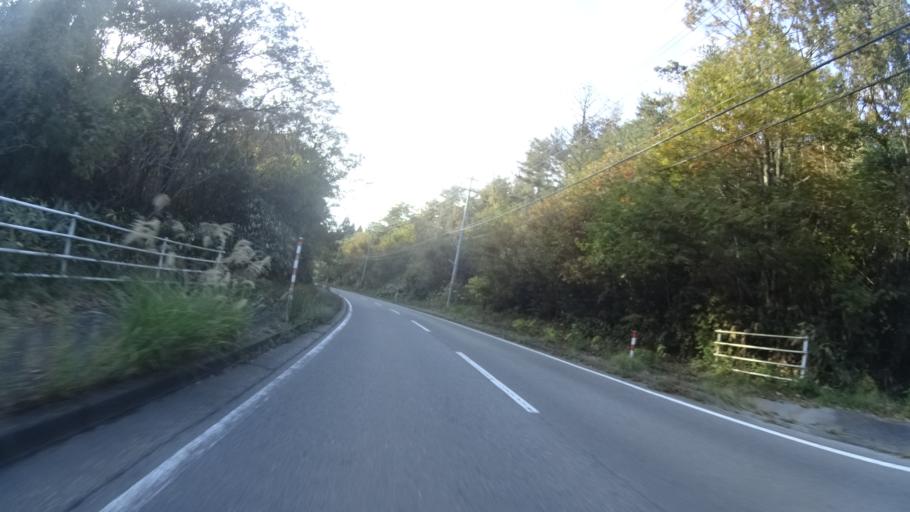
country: JP
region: Ishikawa
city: Hakui
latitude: 37.0656
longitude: 136.7705
